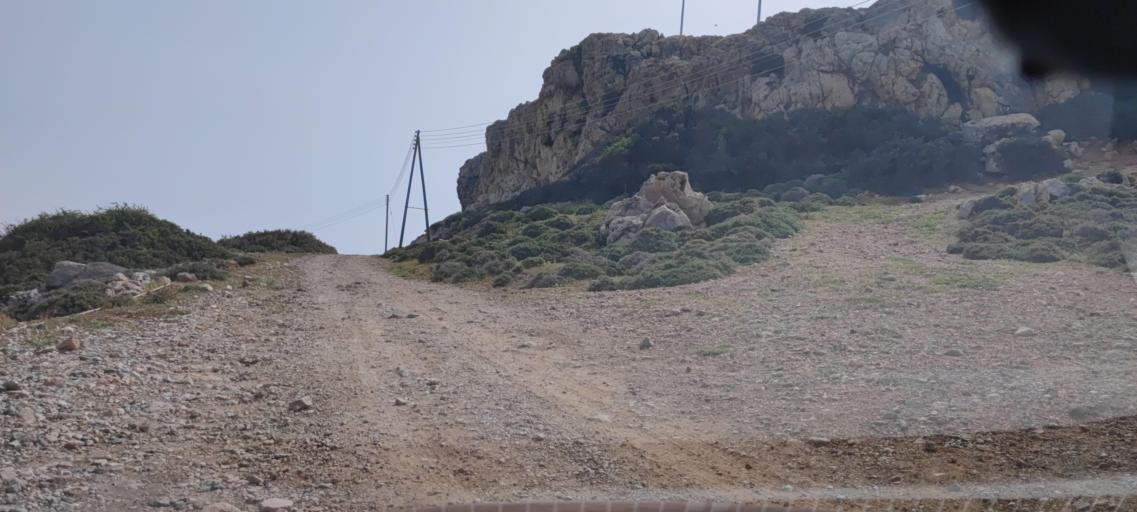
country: CY
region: Ammochostos
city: Rizokarpaso
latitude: 35.6945
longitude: 34.5864
